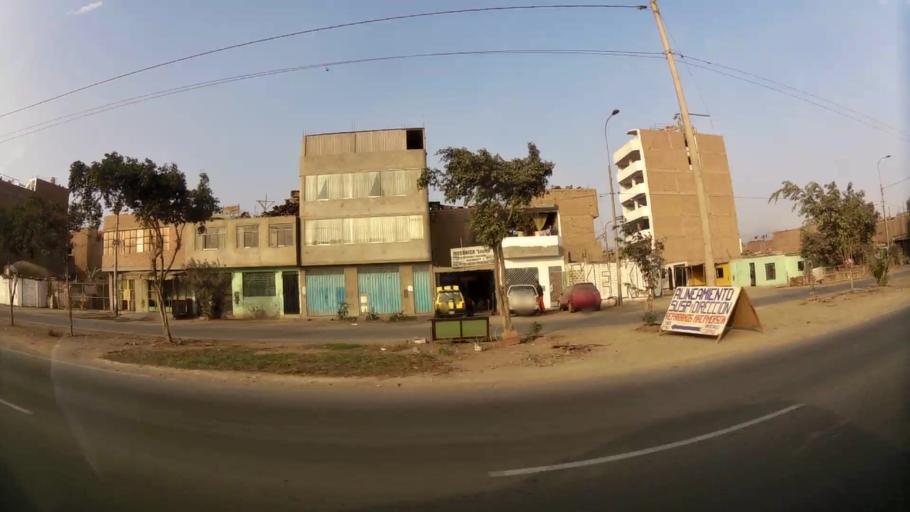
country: PE
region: Lima
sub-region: Lima
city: Independencia
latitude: -11.9596
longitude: -77.0841
